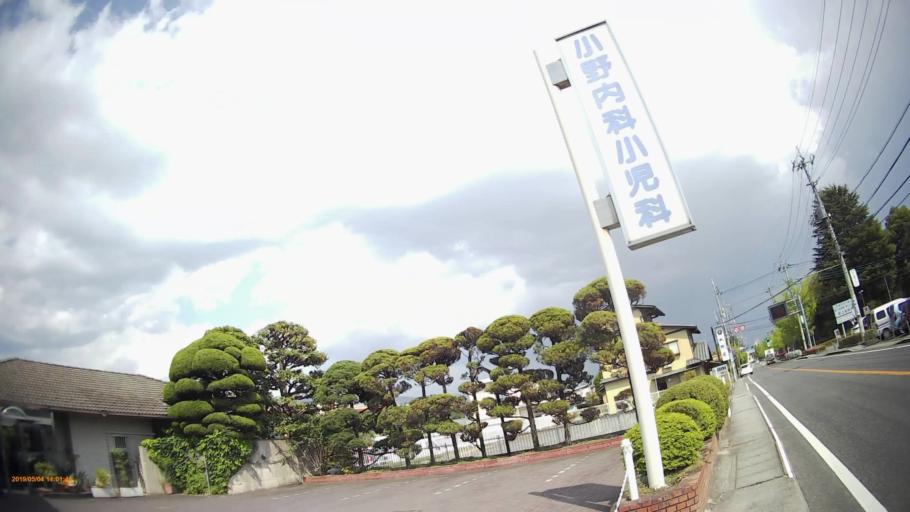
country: JP
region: Yamanashi
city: Kofu-shi
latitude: 35.6621
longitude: 138.5366
